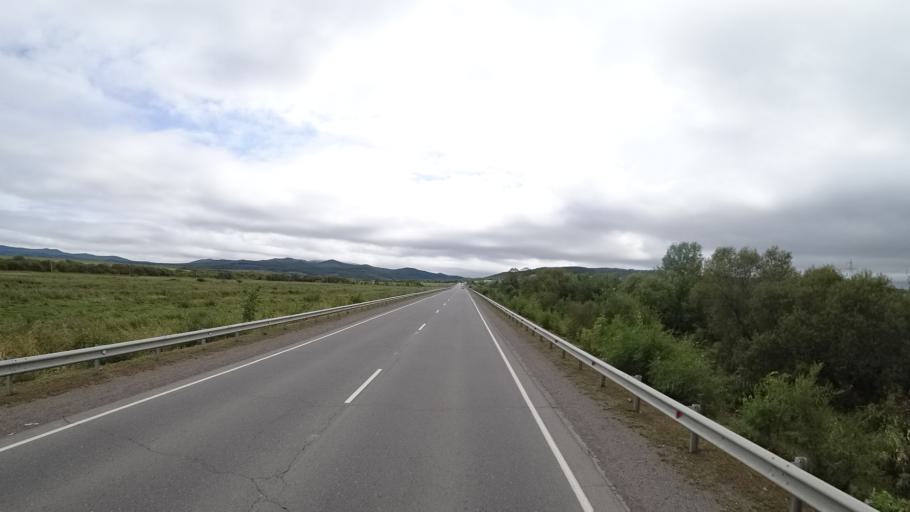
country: RU
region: Primorskiy
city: Monastyrishche
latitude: 44.1797
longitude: 132.4414
